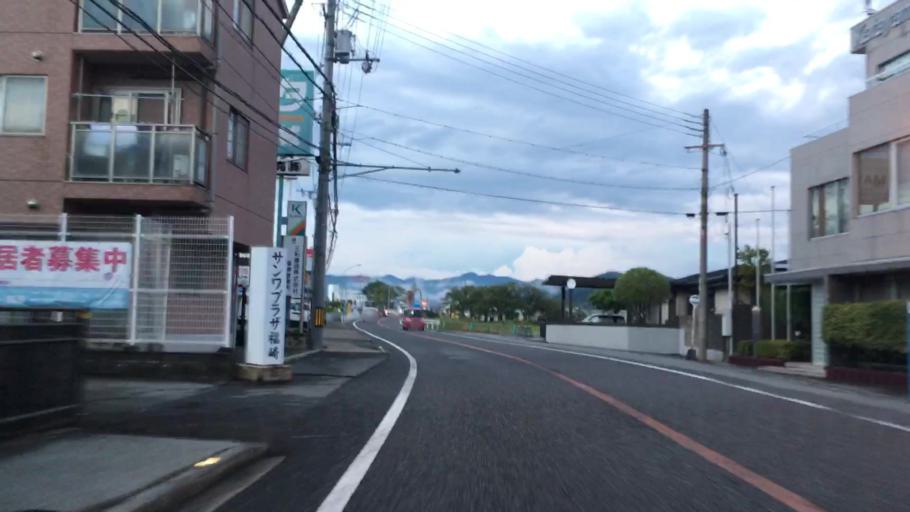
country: JP
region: Hyogo
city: Himeji
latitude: 34.9461
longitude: 134.7475
